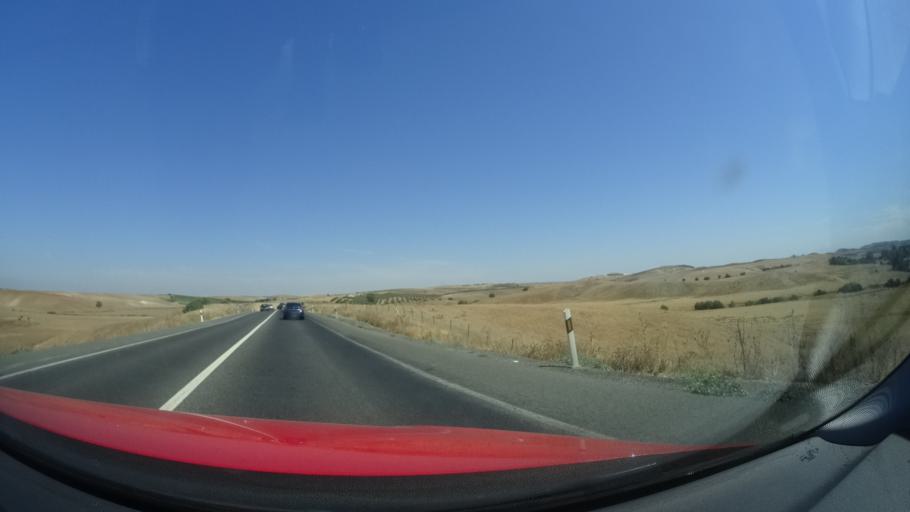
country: ES
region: Andalusia
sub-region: Provincia de Sevilla
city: Las Cabezas de San Juan
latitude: 36.9478
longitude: -5.9033
